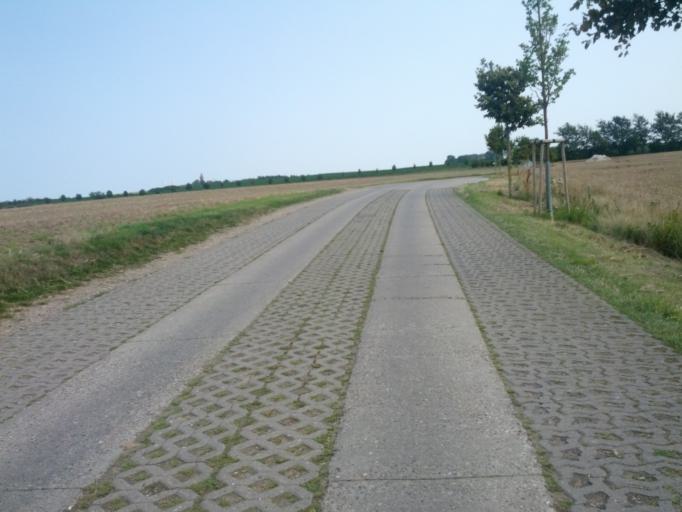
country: DE
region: Mecklenburg-Vorpommern
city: Bastorf
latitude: 54.1294
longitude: 11.6769
